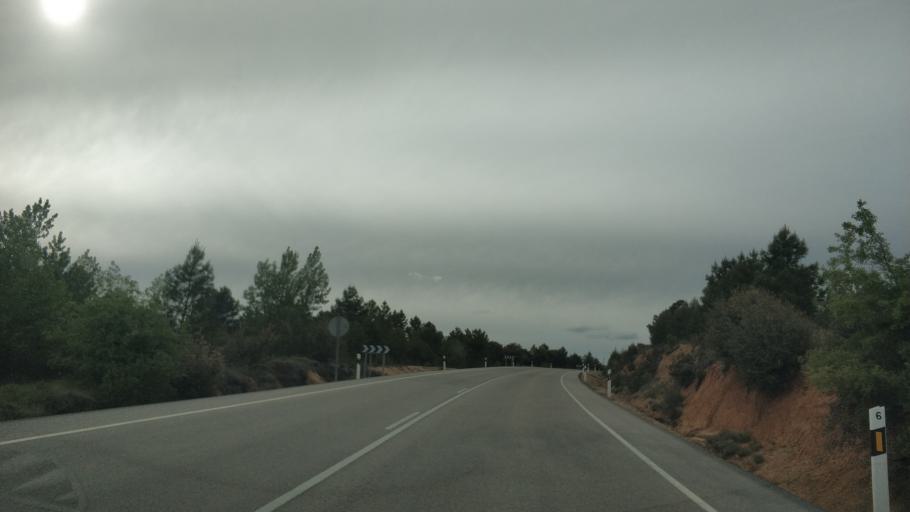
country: ES
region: Castille and Leon
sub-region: Provincia de Soria
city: Quintanas de Gormaz
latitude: 41.5247
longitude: -2.9411
